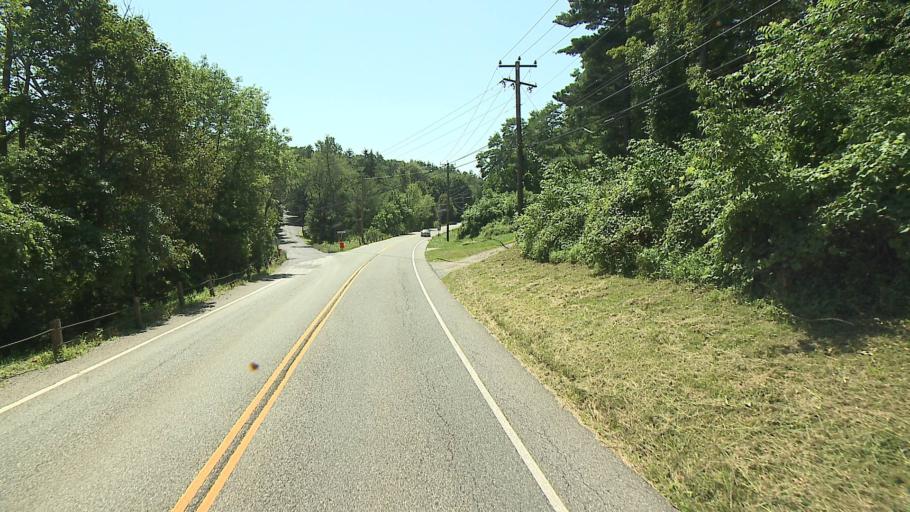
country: US
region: Connecticut
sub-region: Litchfield County
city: Kent
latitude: 41.8738
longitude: -73.4658
